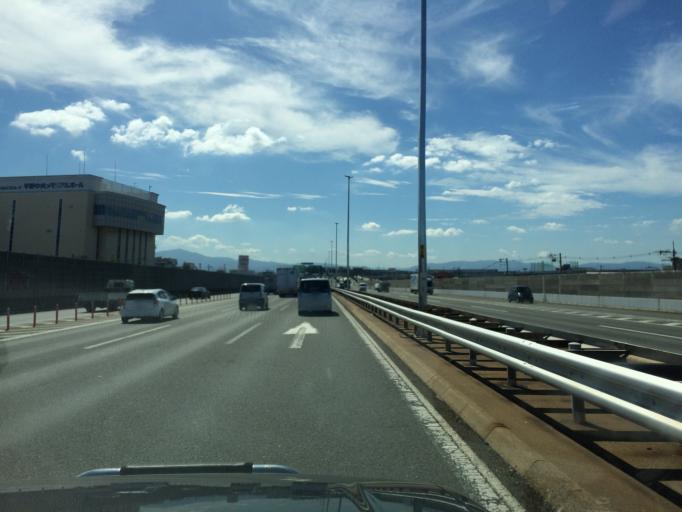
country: JP
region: Osaka
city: Yao
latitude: 34.5982
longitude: 135.5745
